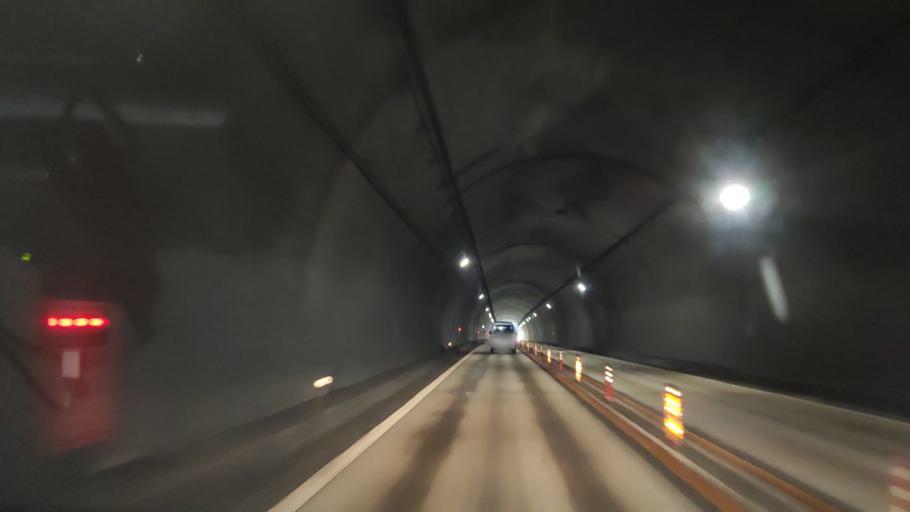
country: JP
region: Tokushima
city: Kamojimacho-jogejima
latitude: 34.1119
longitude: 134.3206
